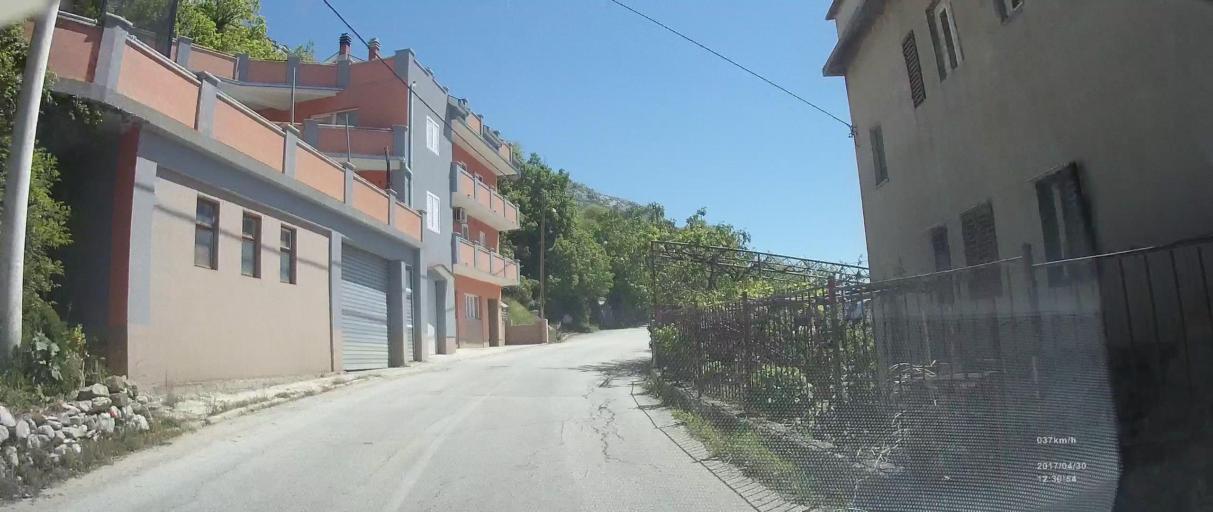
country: HR
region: Splitsko-Dalmatinska
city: Srinjine
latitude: 43.4995
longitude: 16.6091
